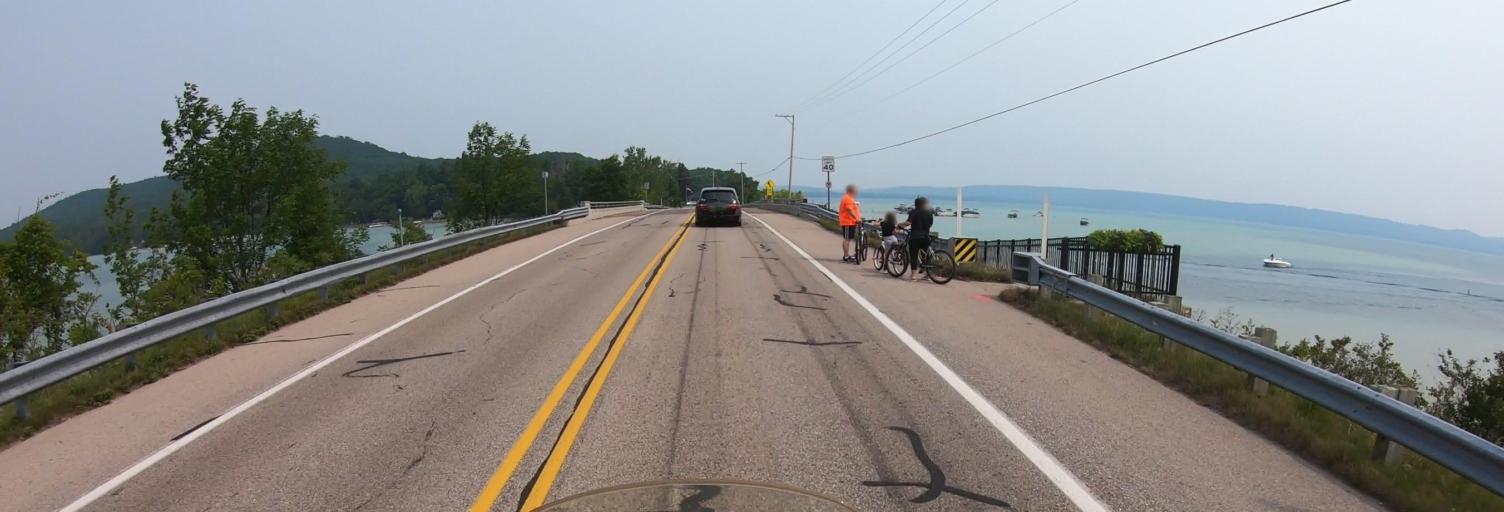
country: US
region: Michigan
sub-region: Benzie County
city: Beulah
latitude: 44.8603
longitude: -85.9963
